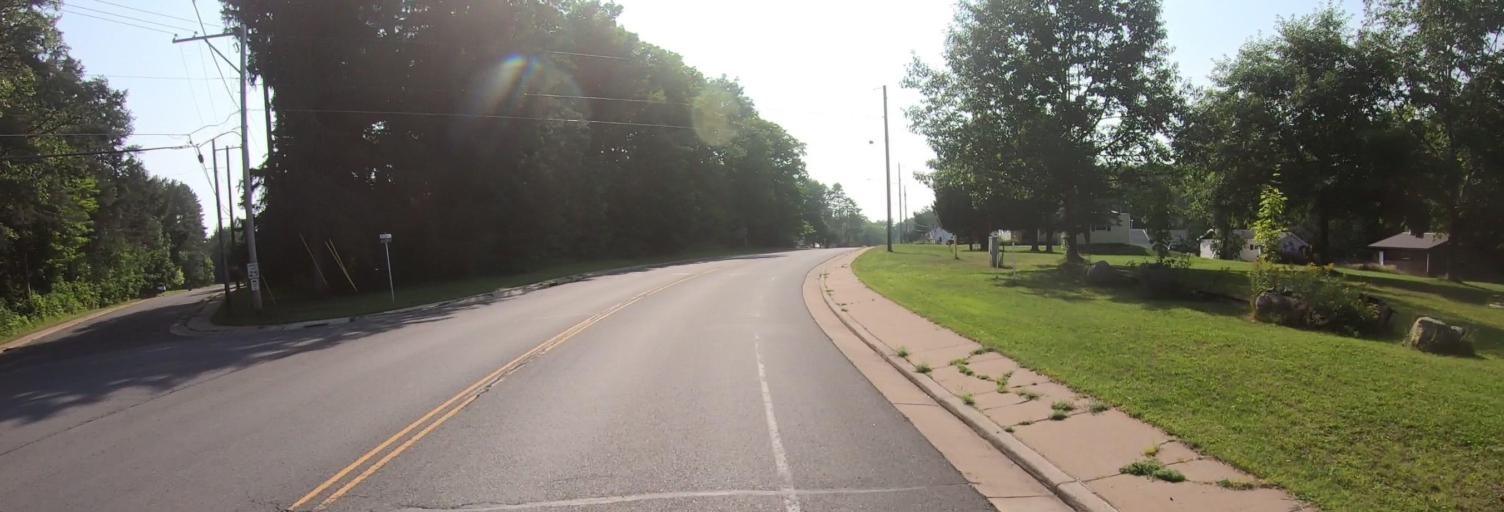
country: US
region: Wisconsin
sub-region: Iron County
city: Hurley
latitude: 46.4274
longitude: -90.2485
